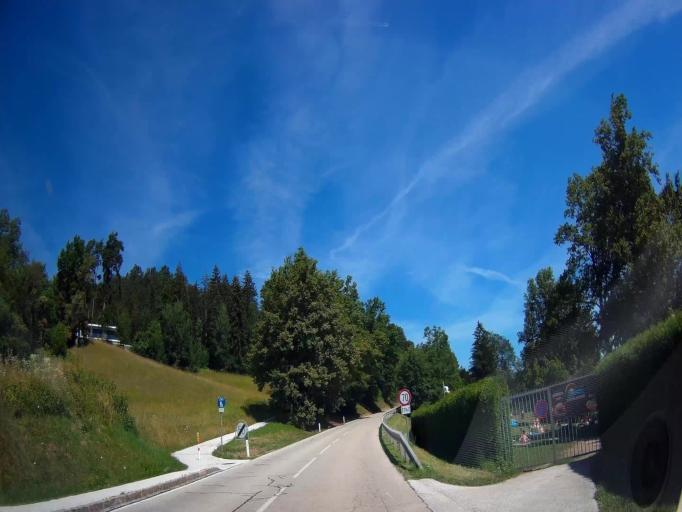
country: AT
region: Carinthia
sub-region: Politischer Bezirk Sankt Veit an der Glan
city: St. Georgen am Laengsee
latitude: 46.7857
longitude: 14.4193
